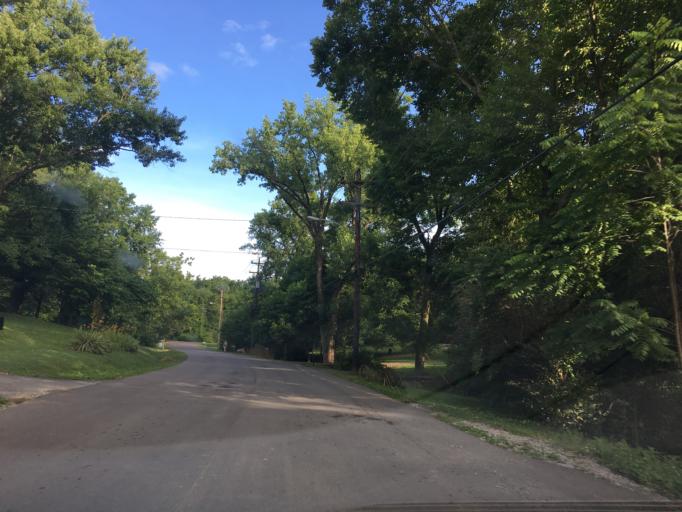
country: US
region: Tennessee
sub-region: Davidson County
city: Oak Hill
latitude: 36.0668
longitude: -86.7334
